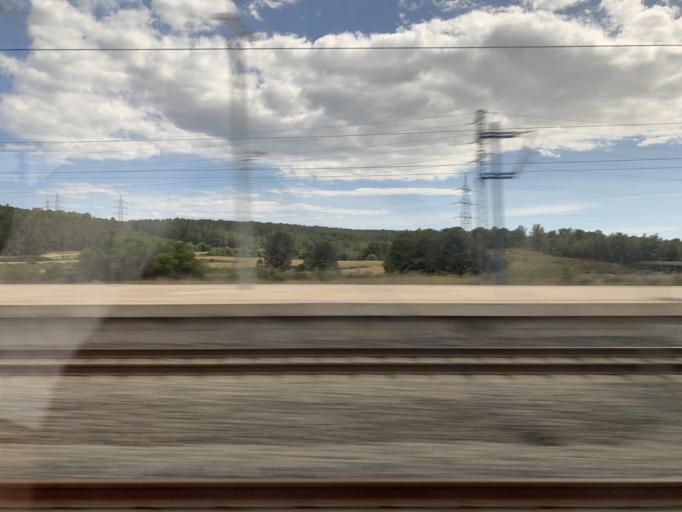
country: ES
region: Catalonia
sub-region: Provincia de Tarragona
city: La Secuita
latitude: 41.1924
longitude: 1.2697
